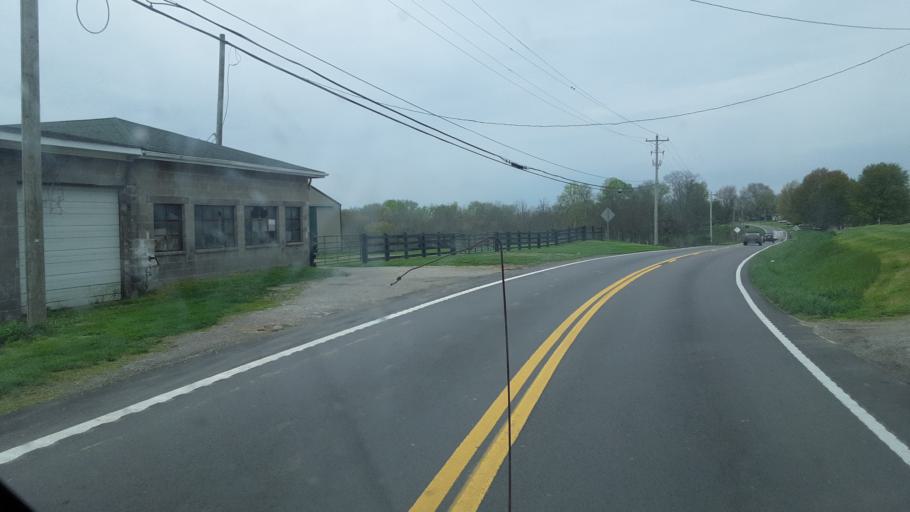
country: US
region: Kentucky
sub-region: Grant County
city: Dry Ridge
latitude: 38.6790
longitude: -84.6152
